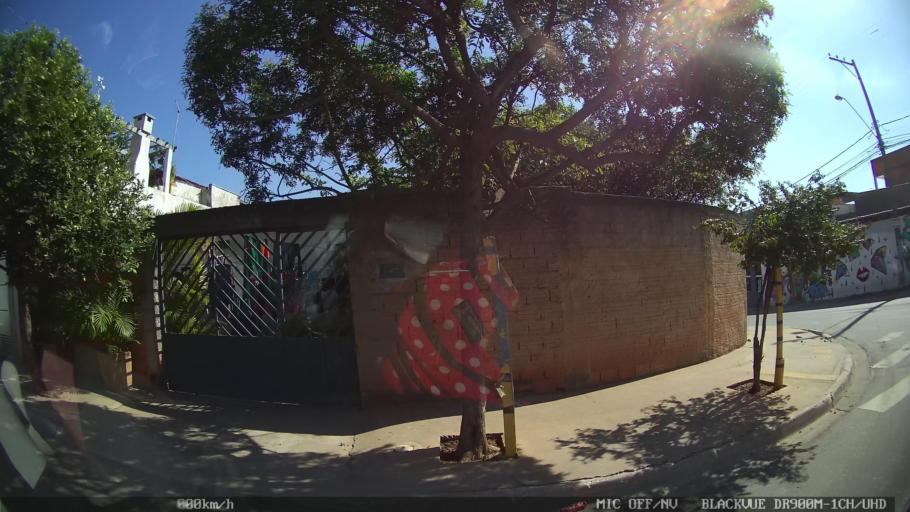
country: BR
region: Sao Paulo
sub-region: Campinas
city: Campinas
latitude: -22.9410
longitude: -47.0820
